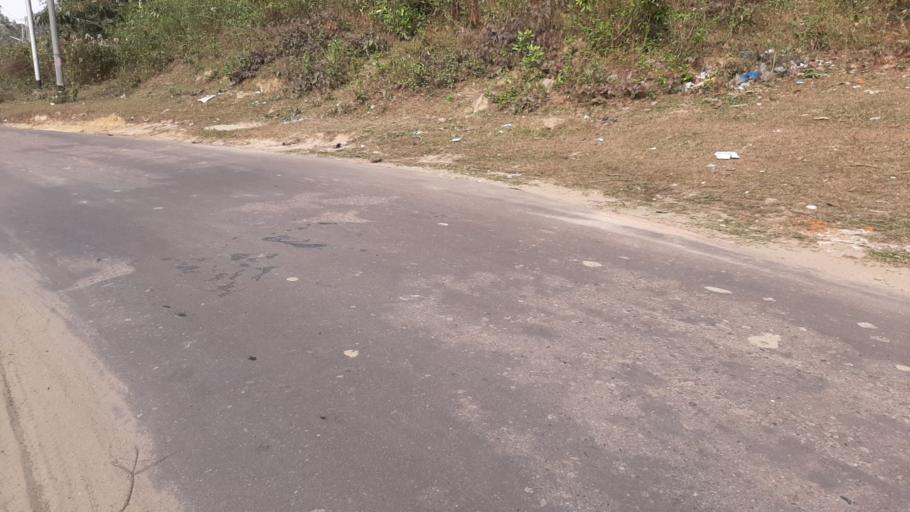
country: BD
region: Chittagong
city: Raojan
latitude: 22.4783
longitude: 91.7908
